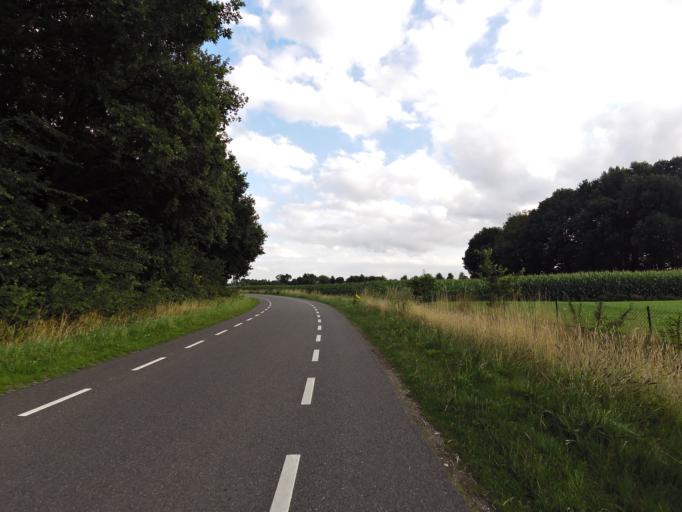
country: NL
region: Gelderland
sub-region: Gemeente Doesburg
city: Doesburg
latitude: 51.9726
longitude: 6.1598
